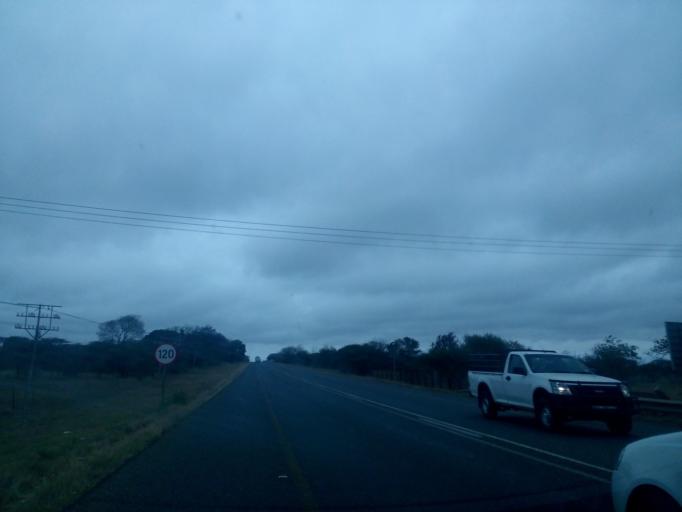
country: ZA
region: Limpopo
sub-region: Vhembe District Municipality
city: Louis Trichardt
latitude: -23.0842
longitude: 29.9067
